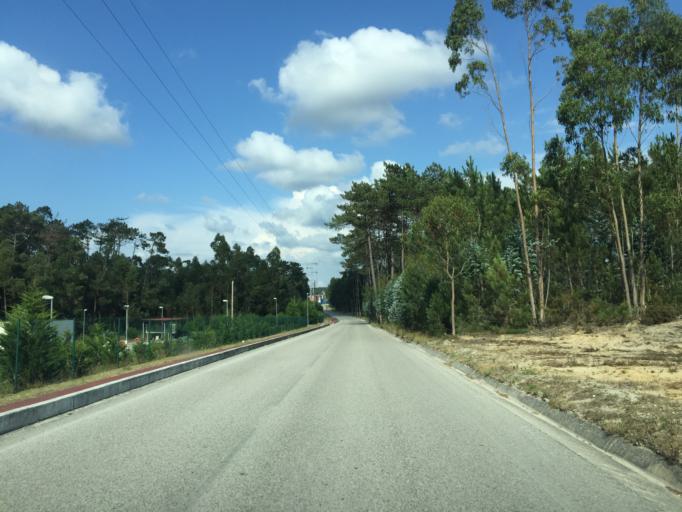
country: PT
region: Leiria
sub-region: Leiria
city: Monte Redondo
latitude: 39.9438
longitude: -8.8166
